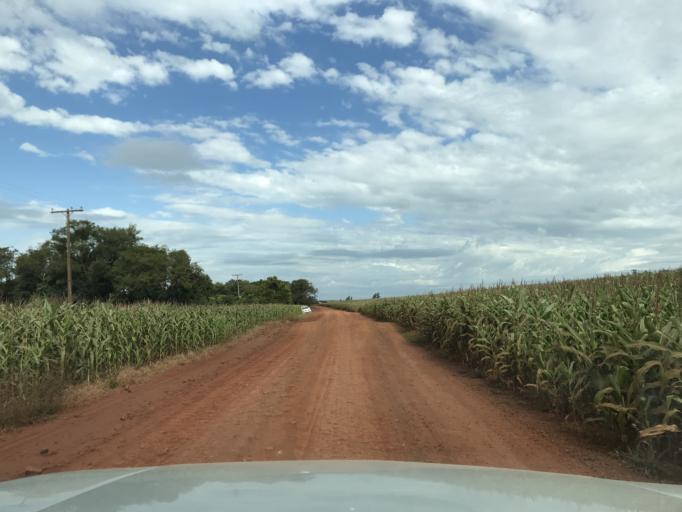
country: BR
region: Parana
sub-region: Palotina
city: Palotina
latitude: -24.3105
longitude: -53.8081
